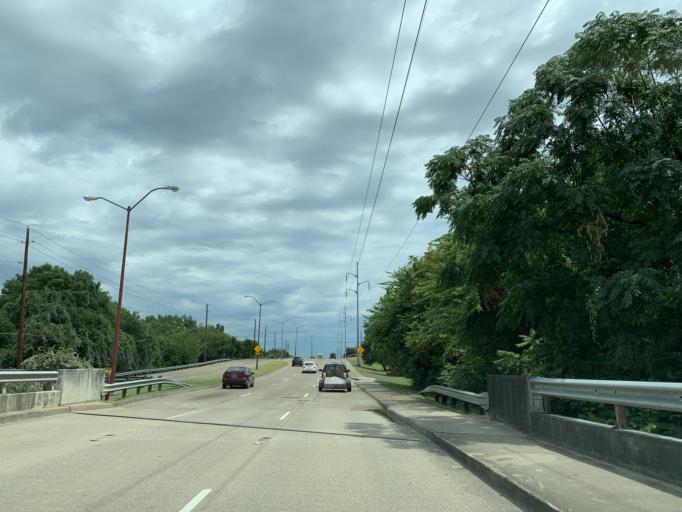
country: US
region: Texas
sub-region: Dallas County
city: DeSoto
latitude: 32.6622
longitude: -96.8143
